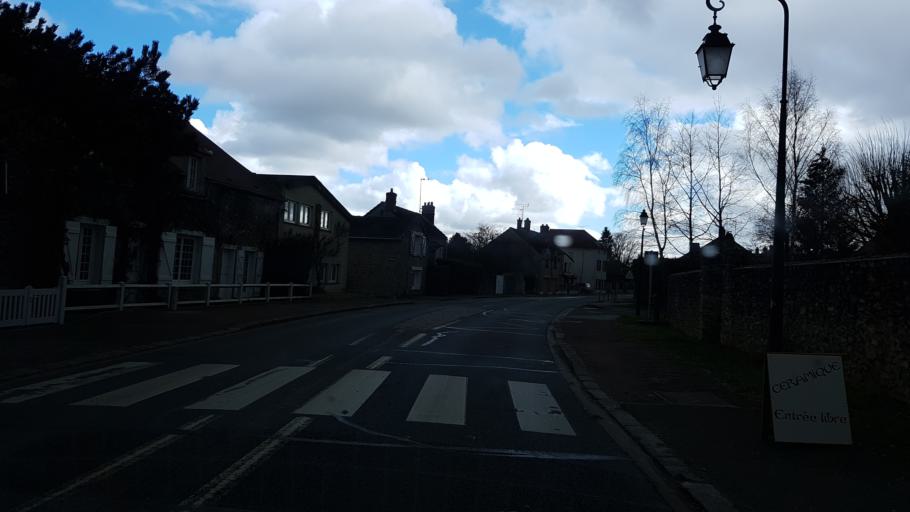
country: FR
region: Ile-de-France
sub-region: Departement des Yvelines
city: Rambouillet
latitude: 48.6155
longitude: 1.8395
